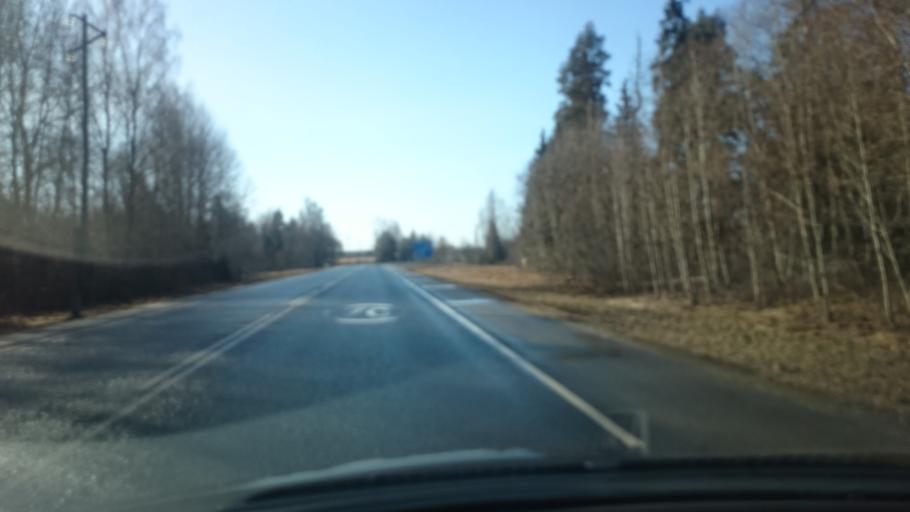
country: EE
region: Raplamaa
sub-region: Rapla vald
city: Rapla
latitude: 59.0444
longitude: 24.8390
